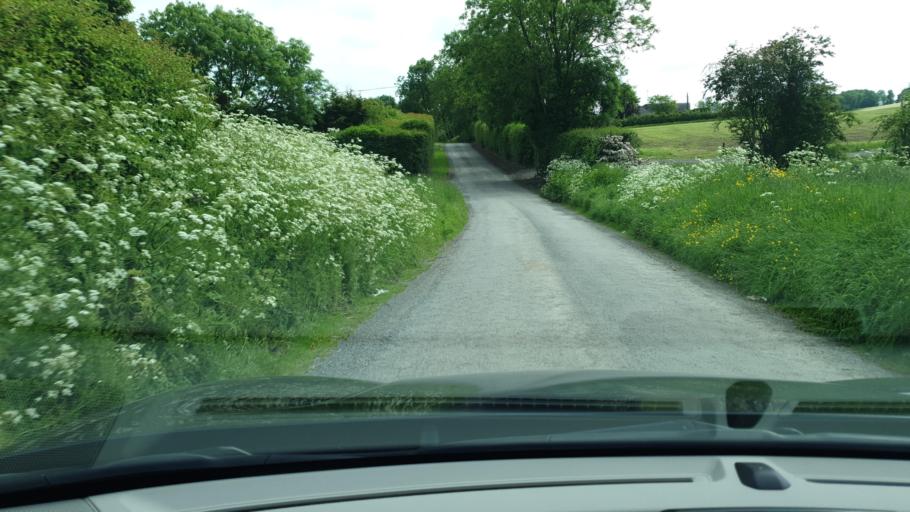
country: IE
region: Ulster
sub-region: An Cabhan
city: Kingscourt
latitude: 53.8027
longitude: -6.7221
